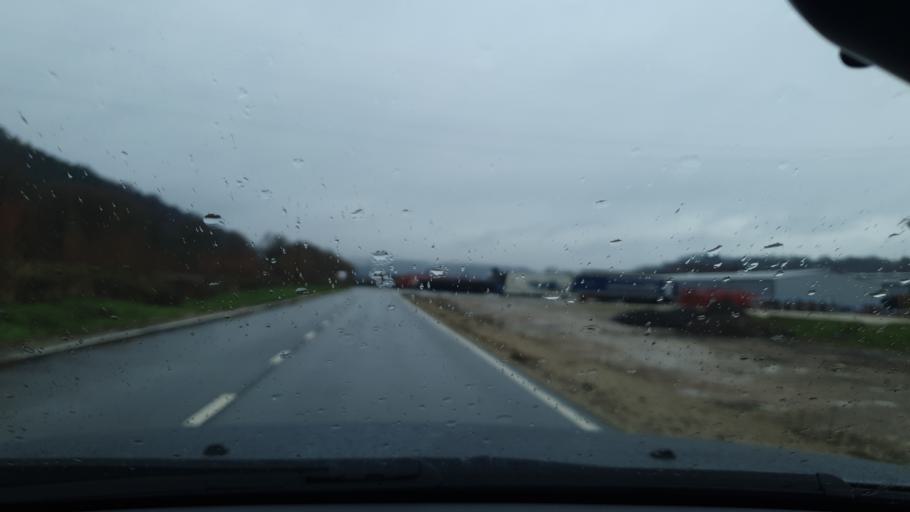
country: DE
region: Rheinland-Pfalz
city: Zweibrucken
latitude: 49.2562
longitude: 7.3340
